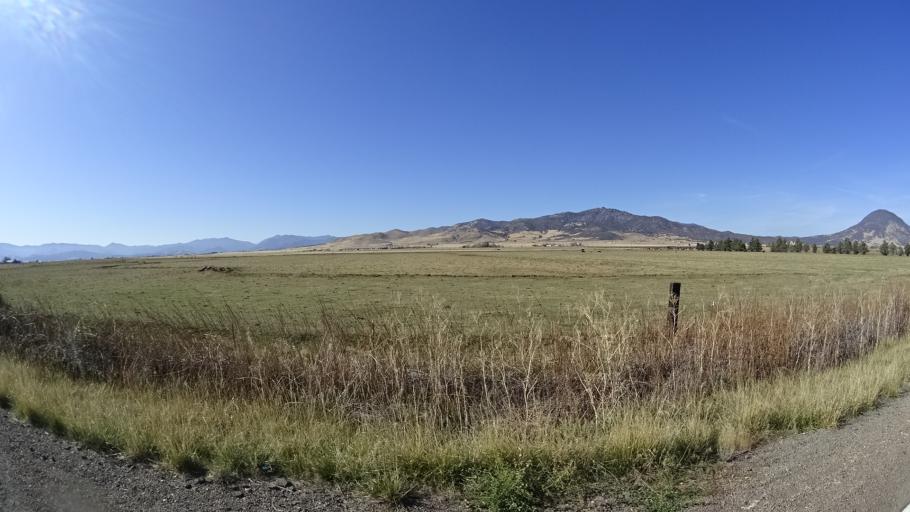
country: US
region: California
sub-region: Siskiyou County
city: Montague
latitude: 41.7842
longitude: -122.4729
